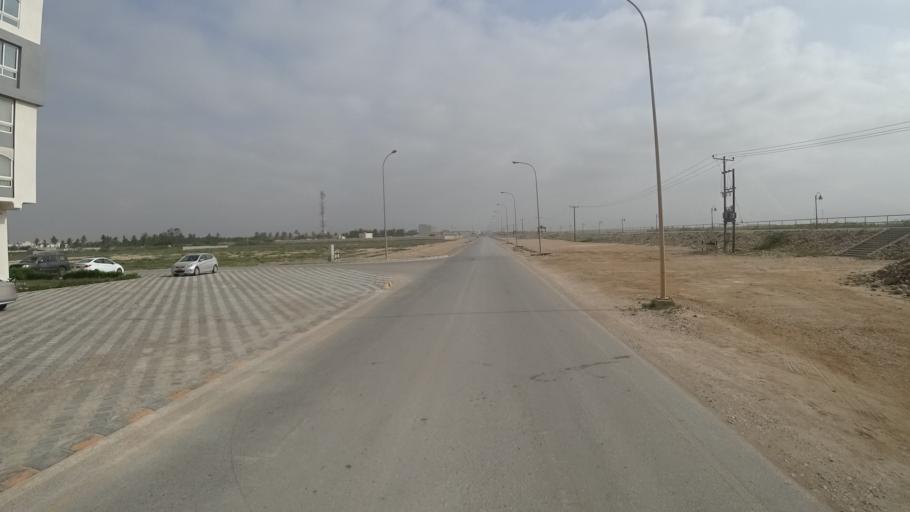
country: OM
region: Zufar
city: Salalah
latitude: 17.0159
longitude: 54.1748
